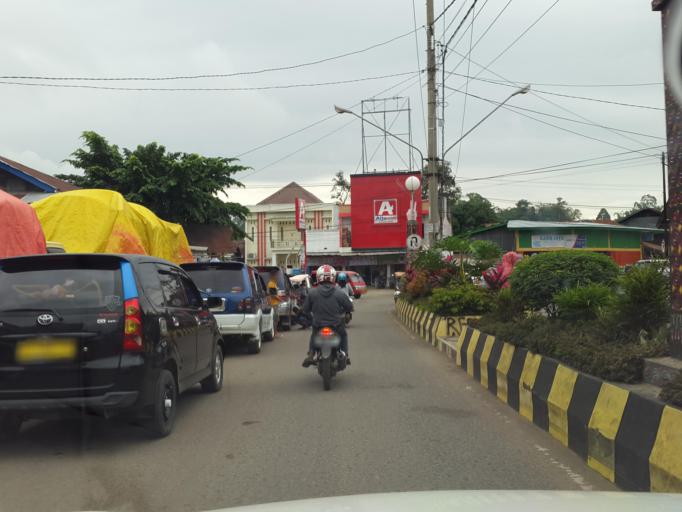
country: ID
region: South Sulawesi
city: Rantepao
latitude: -2.9663
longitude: 119.9005
